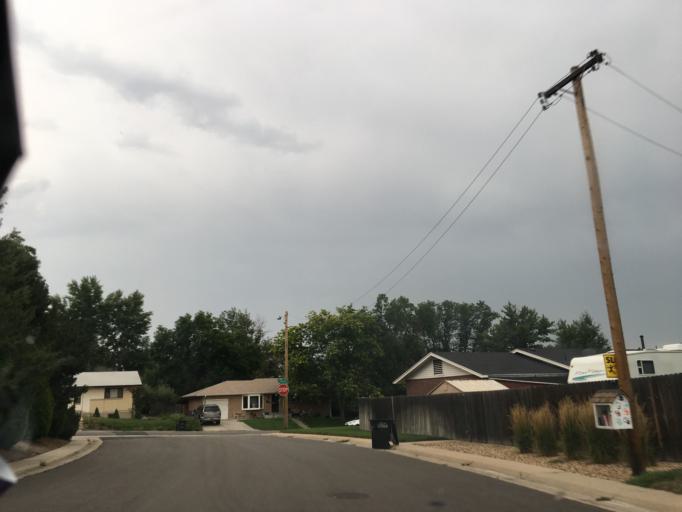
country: US
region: Colorado
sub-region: Arapahoe County
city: Sheridan
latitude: 39.6591
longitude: -105.0420
